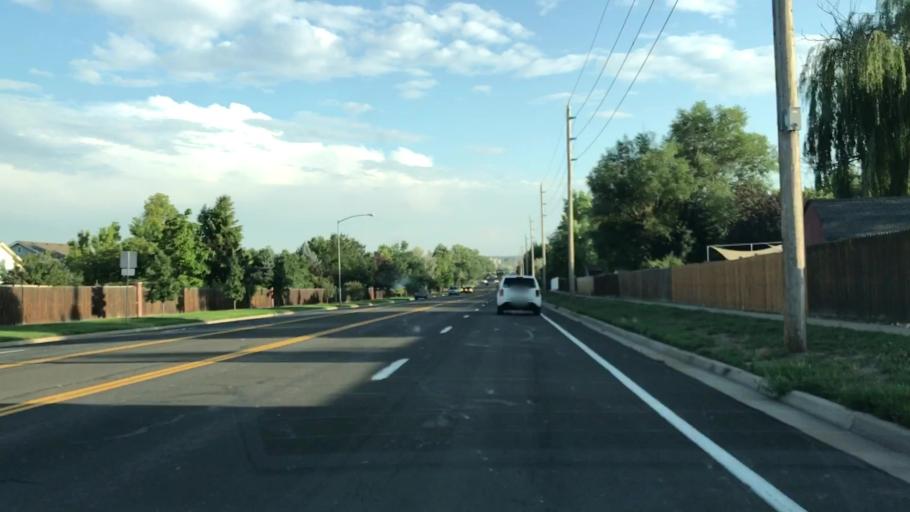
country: US
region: Colorado
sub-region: Adams County
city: Northglenn
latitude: 39.9420
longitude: -105.0157
